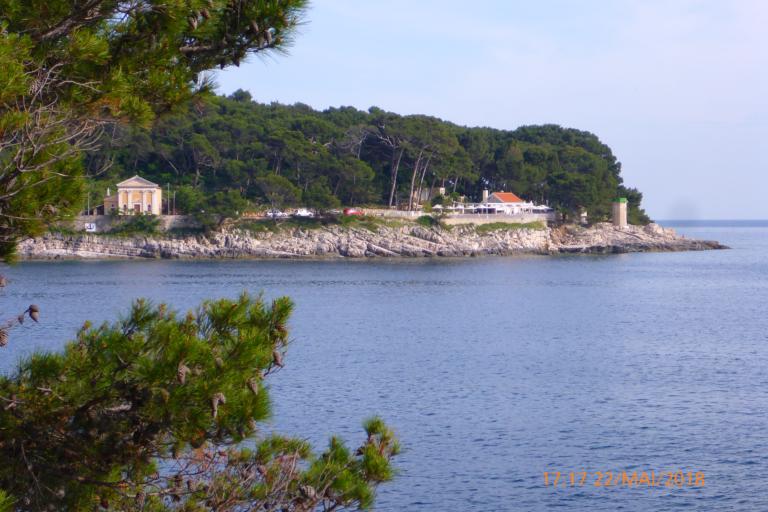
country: HR
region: Primorsko-Goranska
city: Mali Losinj
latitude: 44.5293
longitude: 14.4488
